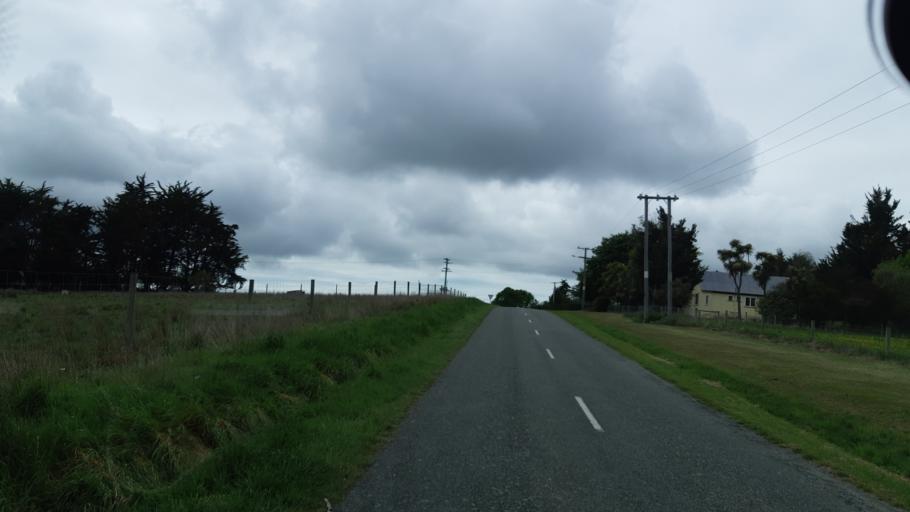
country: NZ
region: Canterbury
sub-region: Timaru District
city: Pleasant Point
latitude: -44.3311
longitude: 171.1560
